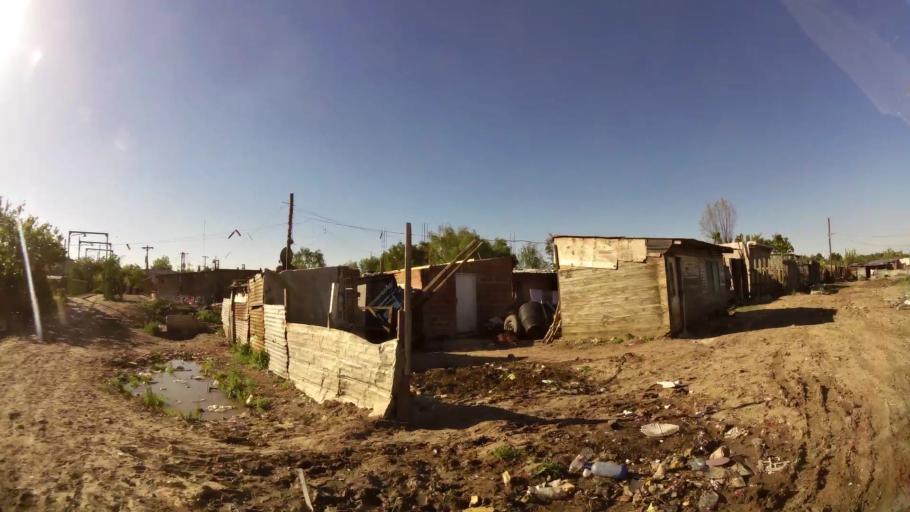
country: AR
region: Buenos Aires
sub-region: Partido de Quilmes
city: Quilmes
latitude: -34.7526
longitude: -58.3196
